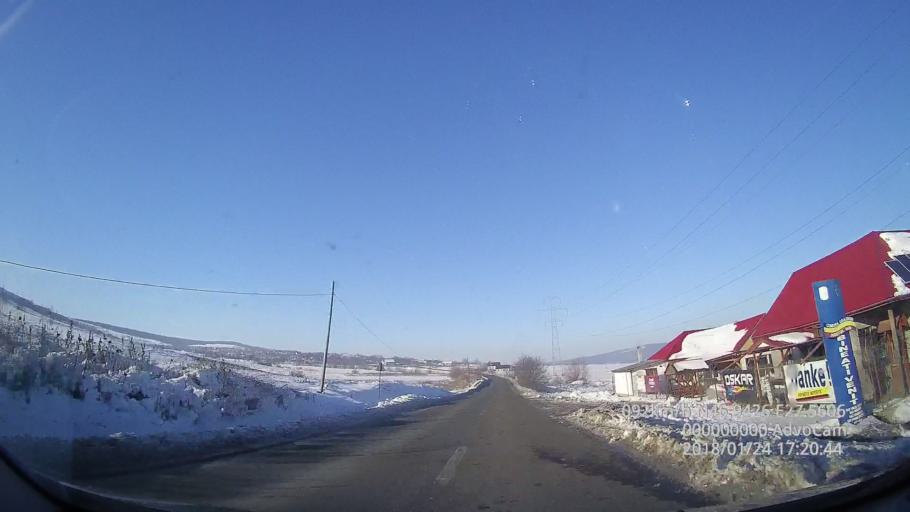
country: RO
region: Iasi
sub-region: Comuna Scanteia
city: Scanteia
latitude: 46.9433
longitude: 27.5604
